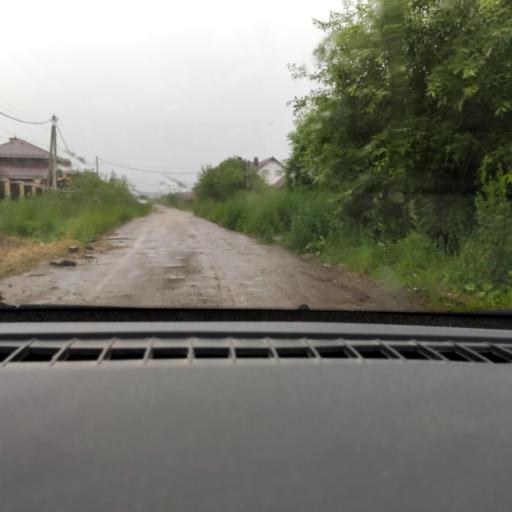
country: RU
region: Perm
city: Perm
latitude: 58.0436
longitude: 56.3747
